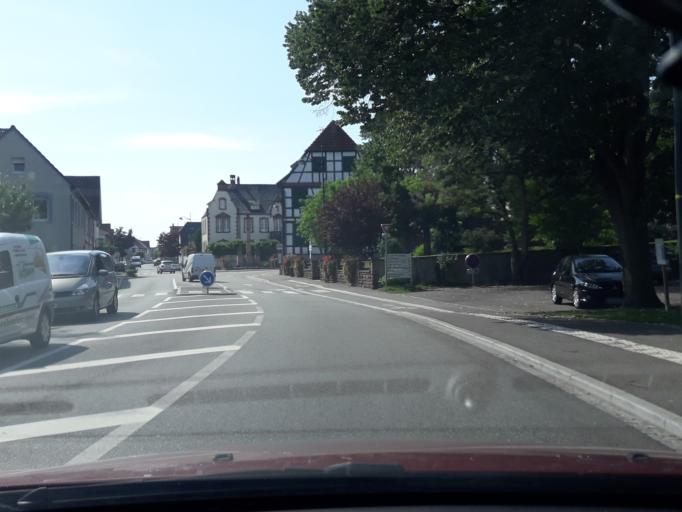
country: FR
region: Alsace
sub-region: Departement du Bas-Rhin
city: Schweighouse-sur-Moder
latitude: 48.8205
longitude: 7.7416
